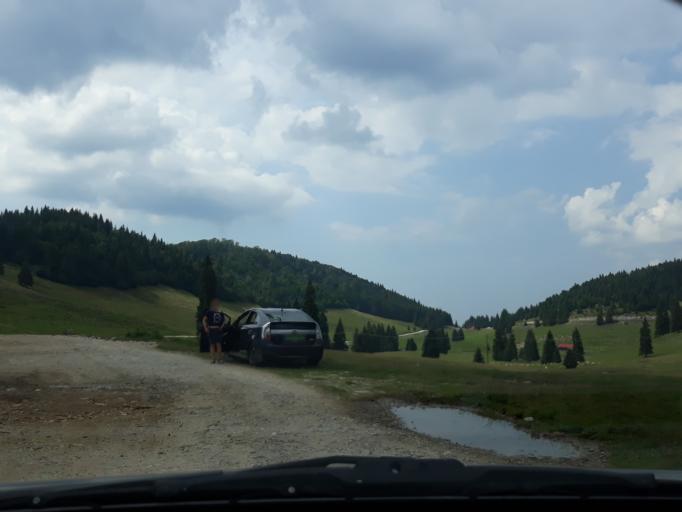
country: RO
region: Alba
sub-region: Comuna Arieseni
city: Arieseni
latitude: 46.5867
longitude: 22.6958
